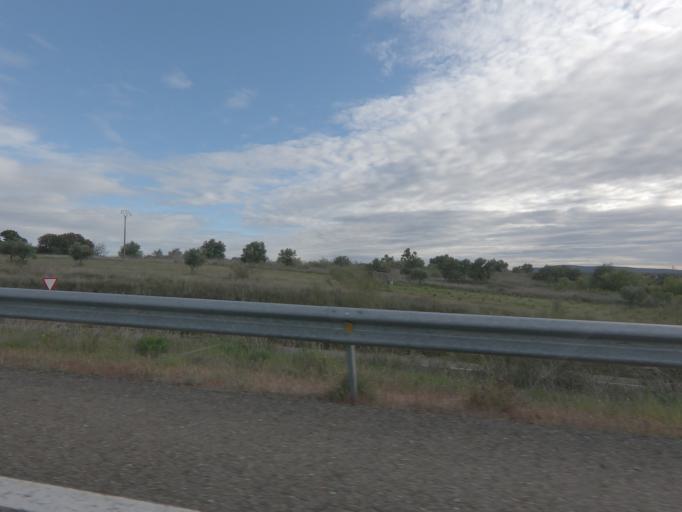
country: ES
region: Extremadura
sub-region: Provincia de Caceres
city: Torrejoncillo
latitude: 39.8845
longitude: -6.4734
